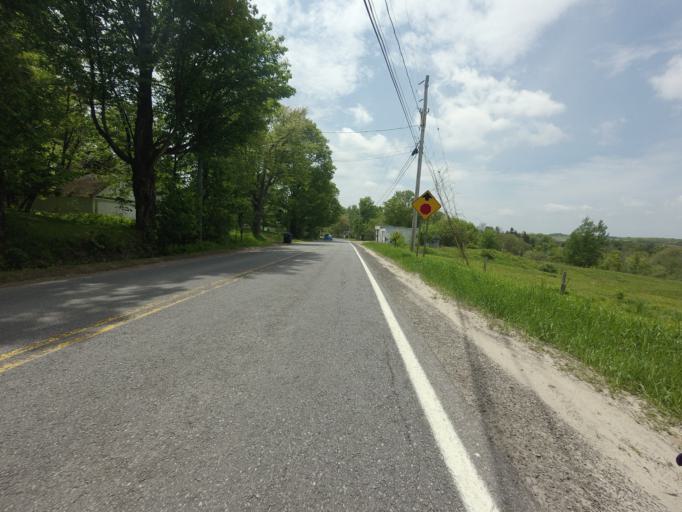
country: US
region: New York
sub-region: St. Lawrence County
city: Hannawa Falls
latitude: 44.5433
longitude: -75.0104
